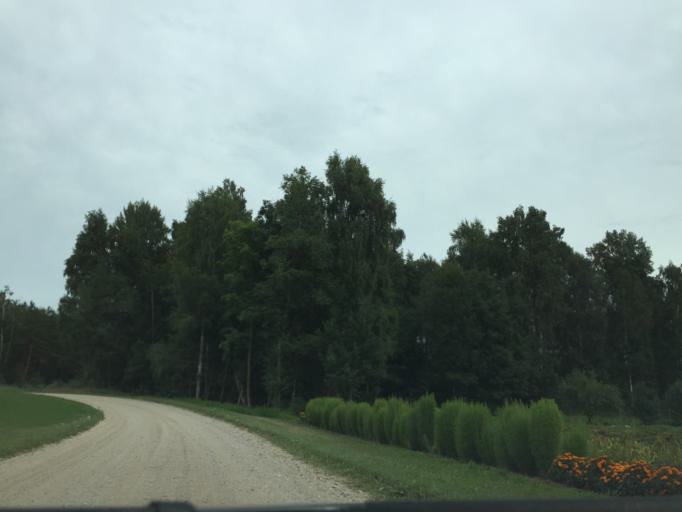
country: LV
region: Jaunpils
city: Jaunpils
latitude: 56.7271
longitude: 23.0730
